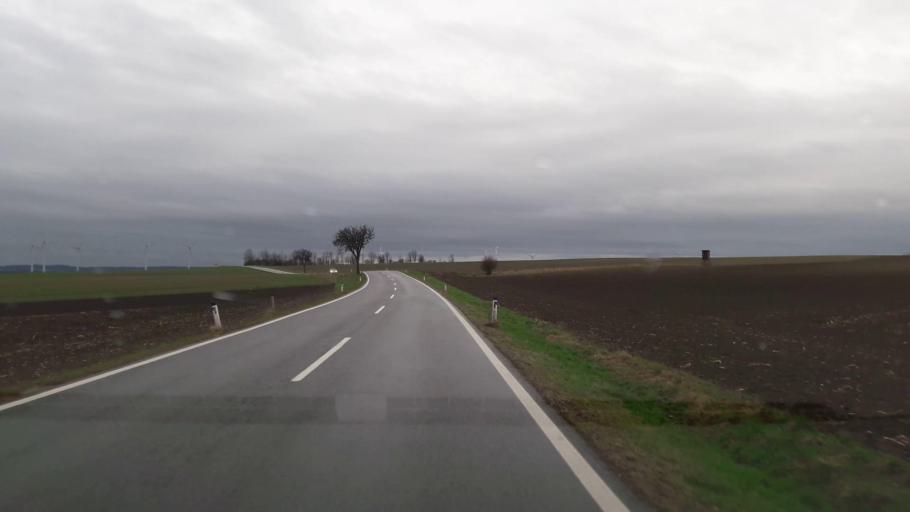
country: AT
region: Lower Austria
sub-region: Politischer Bezirk Bruck an der Leitha
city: Scharndorf
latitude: 48.0857
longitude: 16.7965
